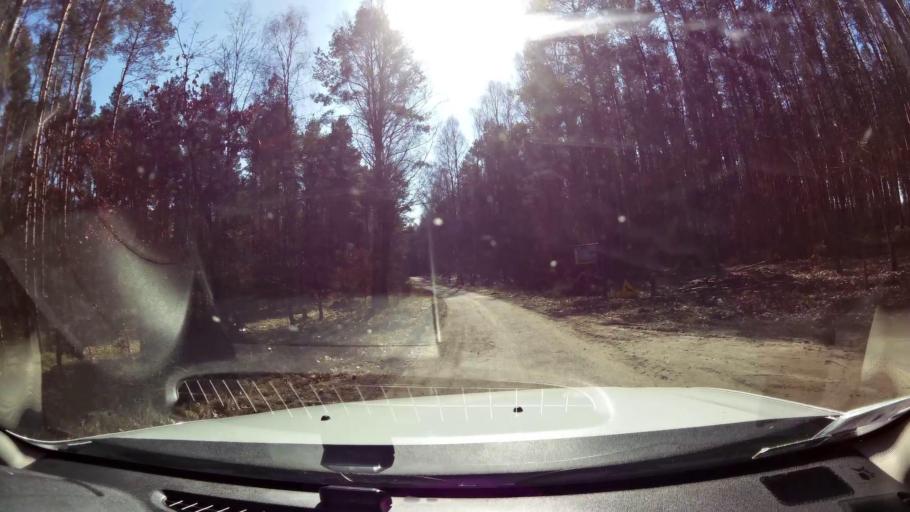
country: PL
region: West Pomeranian Voivodeship
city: Trzcinsko Zdroj
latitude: 53.0326
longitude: 14.6325
